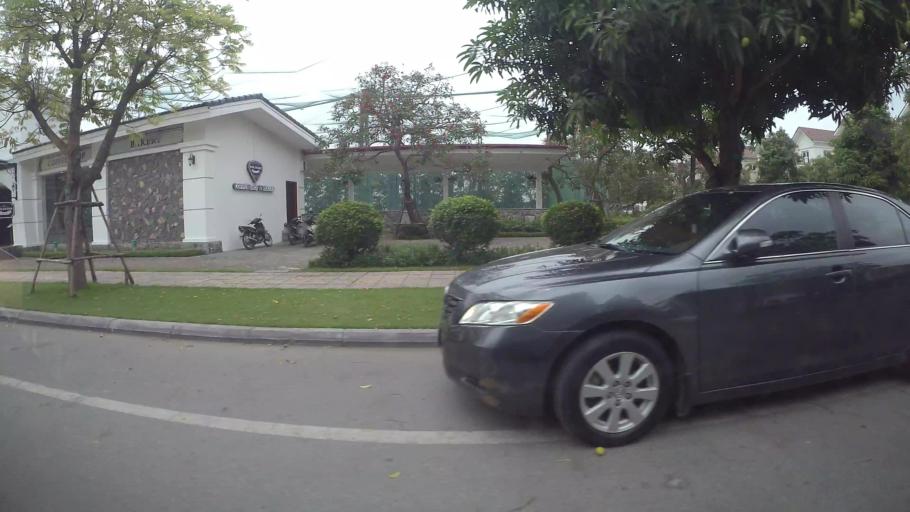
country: VN
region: Ha Noi
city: Trau Quy
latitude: 21.0411
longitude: 105.9176
